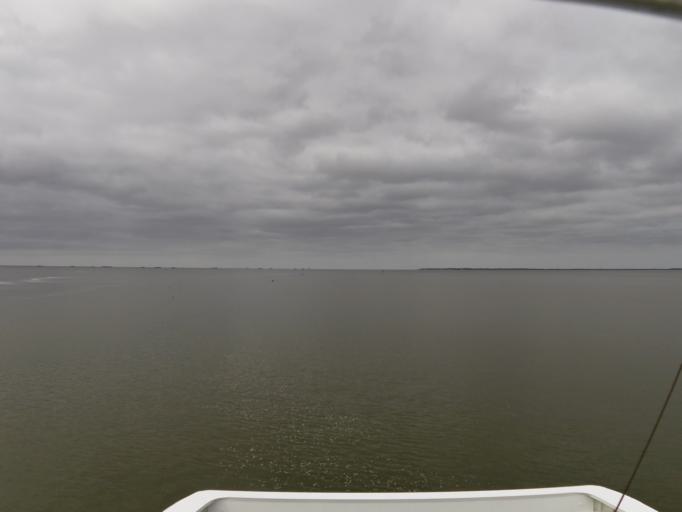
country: DE
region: Schleswig-Holstein
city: Dagebull
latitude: 54.7310
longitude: 8.6859
